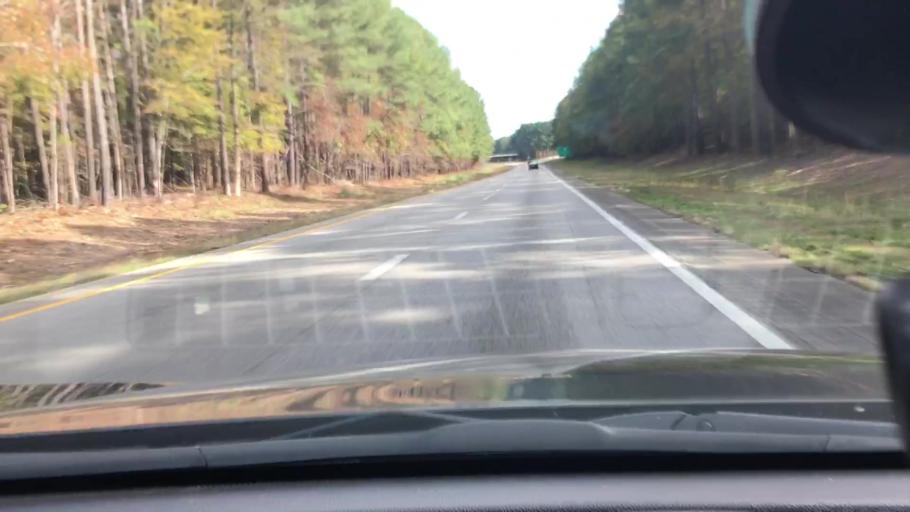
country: US
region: North Carolina
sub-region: Wake County
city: Zebulon
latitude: 35.8020
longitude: -78.1990
